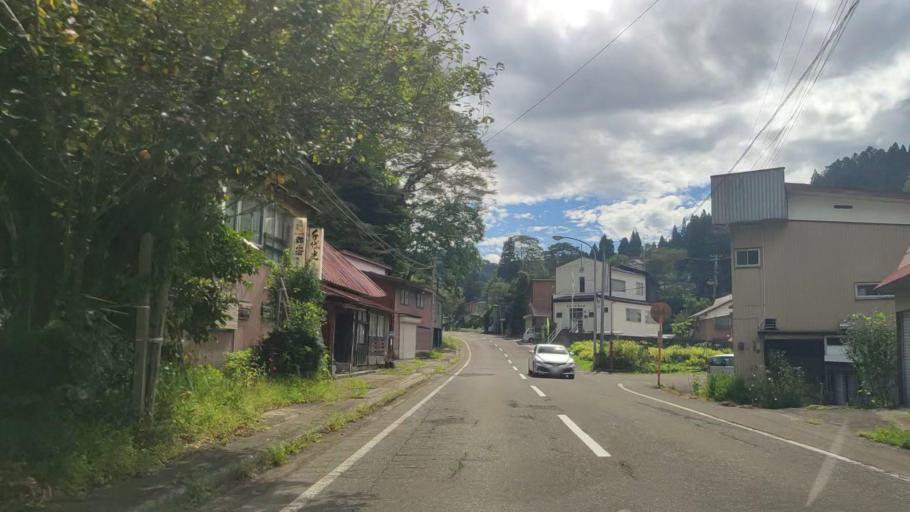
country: JP
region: Niigata
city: Arai
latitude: 36.9288
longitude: 138.2988
